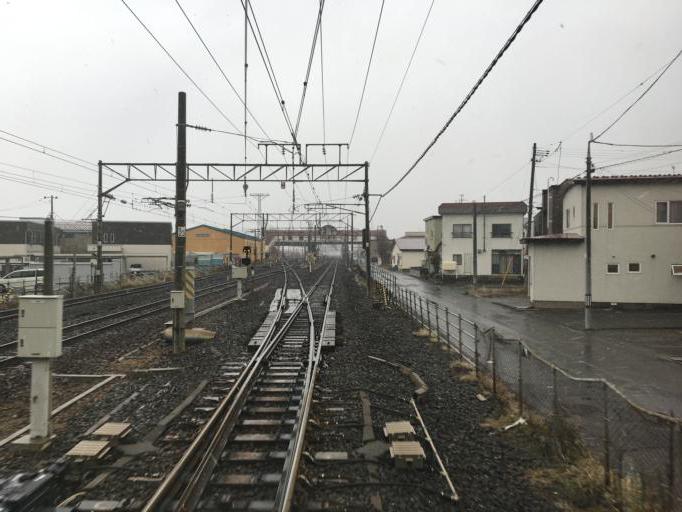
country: JP
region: Aomori
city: Aomori Shi
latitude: 40.8086
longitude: 140.7800
